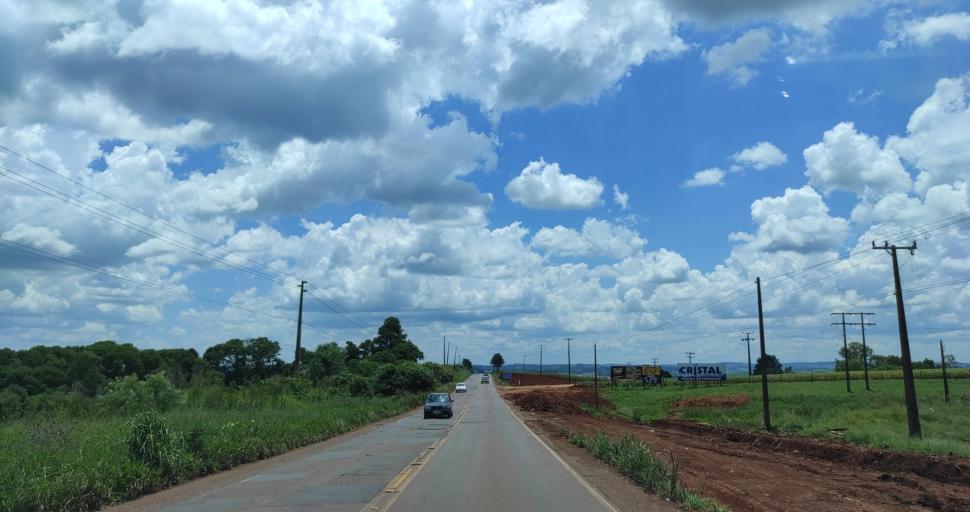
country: BR
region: Santa Catarina
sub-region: Xanxere
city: Xanxere
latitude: -26.7835
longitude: -52.4079
